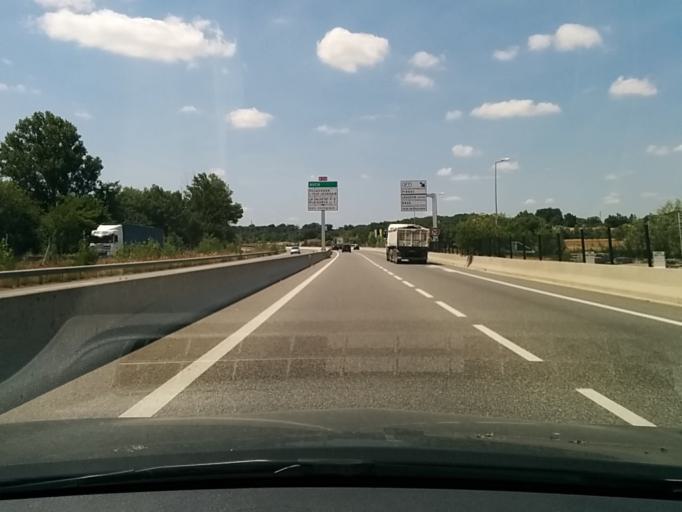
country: FR
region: Midi-Pyrenees
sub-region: Departement de la Haute-Garonne
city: Pibrac
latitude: 43.6052
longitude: 1.2887
